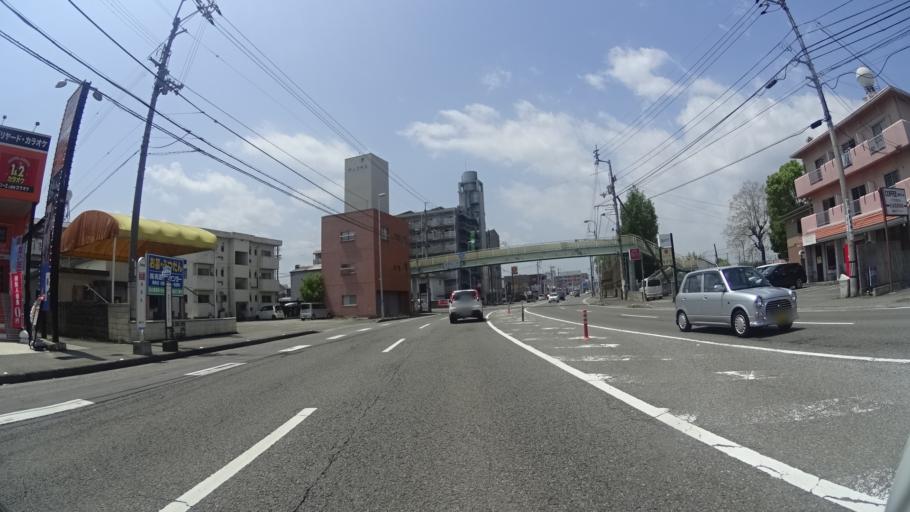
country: JP
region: Tokushima
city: Tokushima-shi
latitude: 34.0726
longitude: 134.5075
